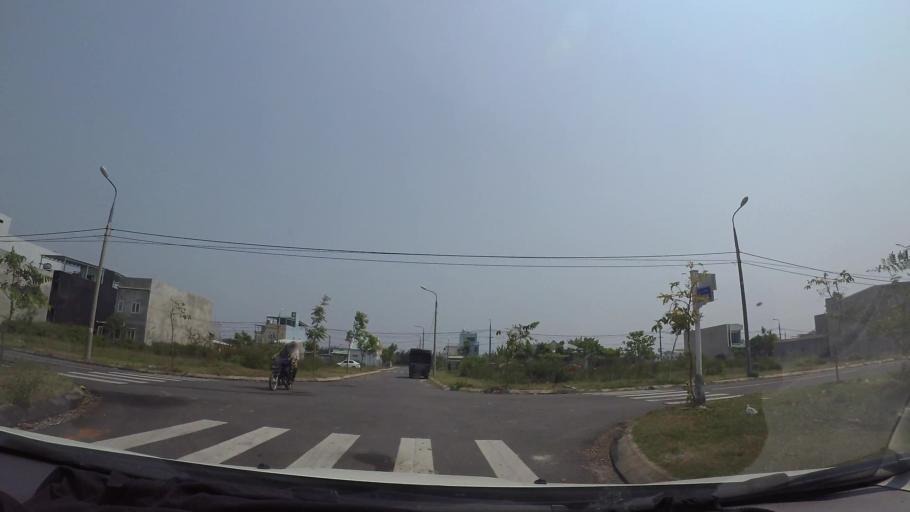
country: VN
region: Da Nang
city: Cam Le
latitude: 15.9904
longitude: 108.2020
